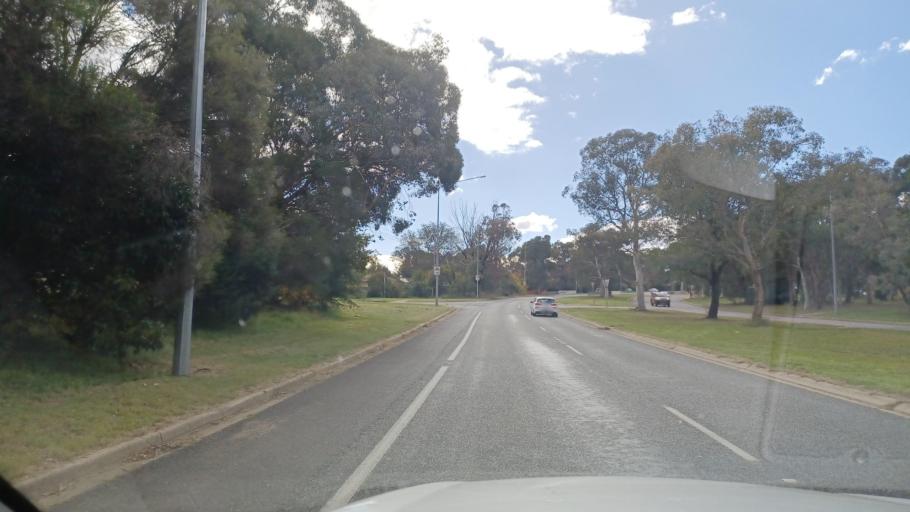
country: AU
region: Australian Capital Territory
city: Belconnen
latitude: -35.2100
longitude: 149.0479
